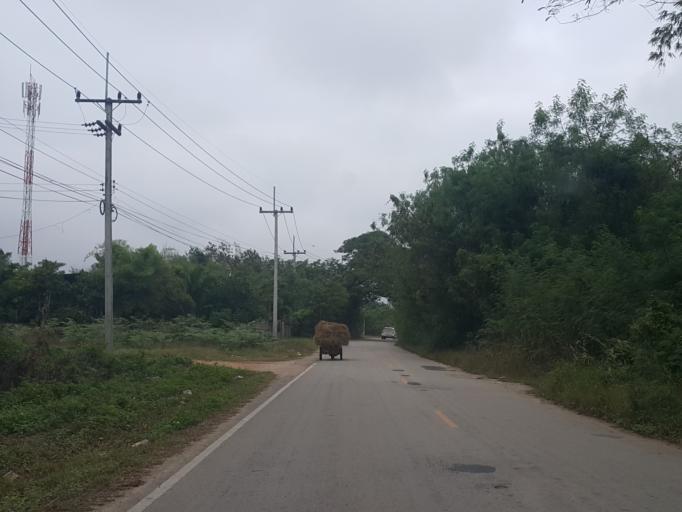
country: TH
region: Lampang
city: Lampang
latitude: 18.3266
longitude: 99.4873
